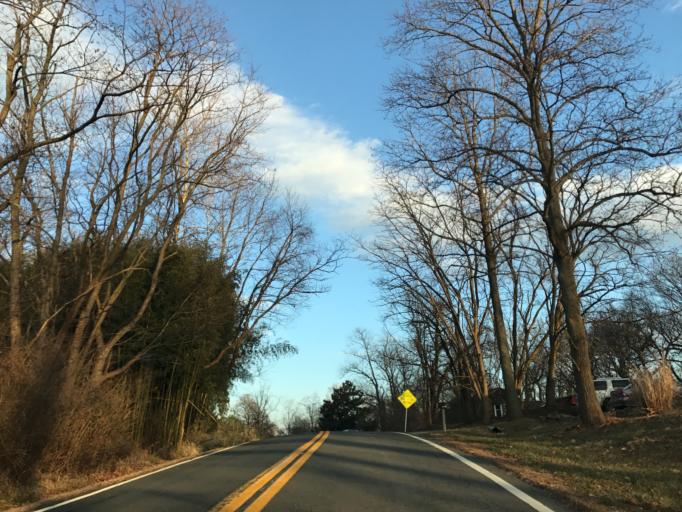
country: US
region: Maryland
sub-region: Cecil County
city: Charlestown
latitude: 39.4623
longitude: -76.0004
